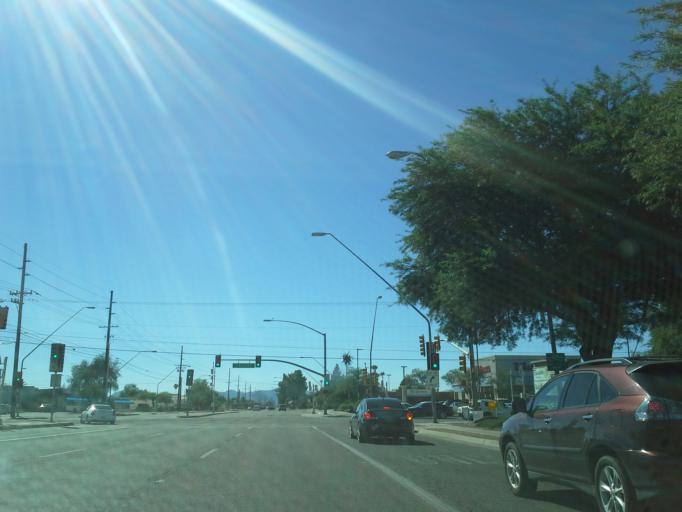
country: US
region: Arizona
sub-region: Pima County
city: Tucson
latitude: 32.2508
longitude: -110.8919
